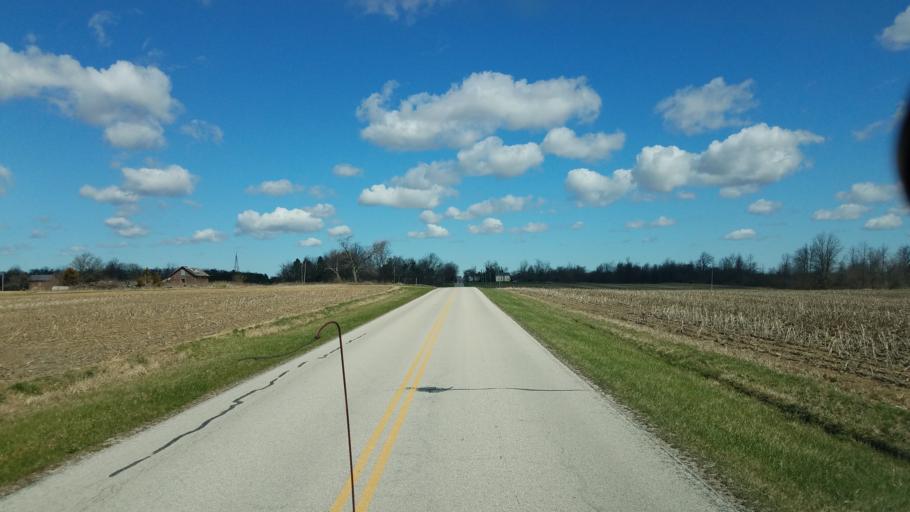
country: US
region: Ohio
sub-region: Sandusky County
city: Mount Carmel
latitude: 41.1586
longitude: -82.9381
